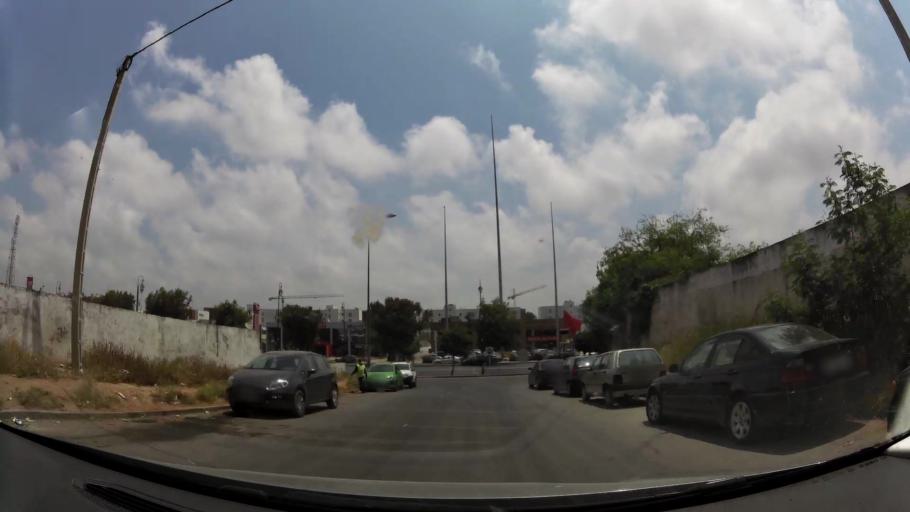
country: MA
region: Rabat-Sale-Zemmour-Zaer
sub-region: Rabat
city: Rabat
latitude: 33.9793
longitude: -6.8756
